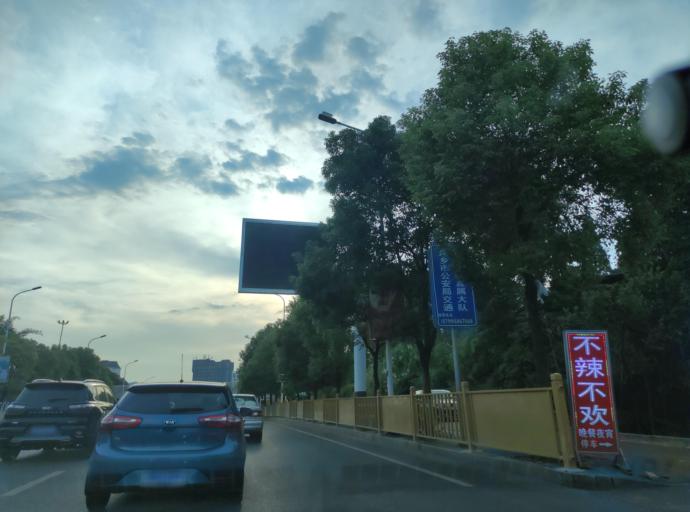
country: CN
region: Jiangxi Sheng
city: Pingxiang
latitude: 27.6338
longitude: 113.8617
